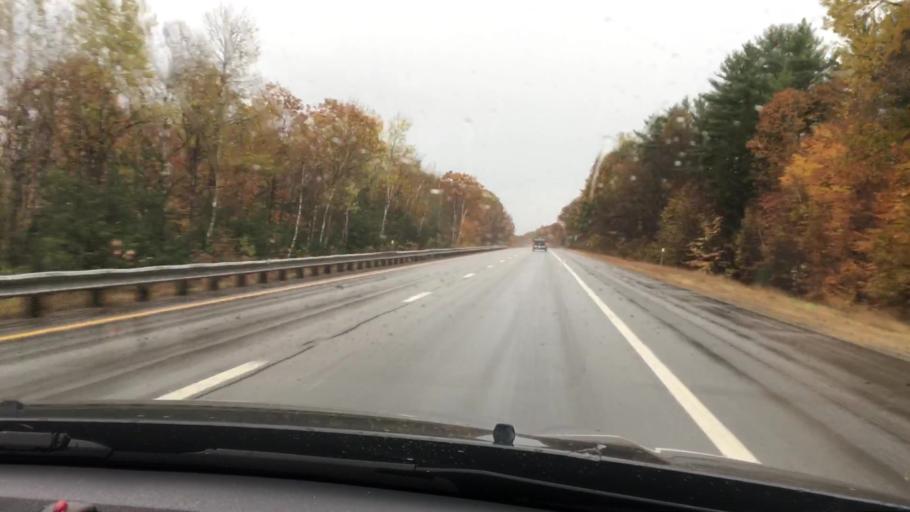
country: US
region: New Hampshire
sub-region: Belknap County
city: Sanbornton
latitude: 43.5527
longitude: -71.6175
